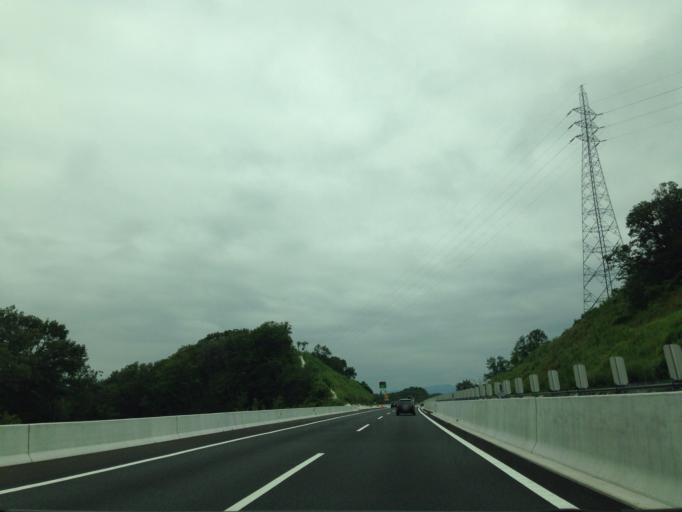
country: JP
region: Aichi
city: Okazaki
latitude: 34.9926
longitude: 137.2335
